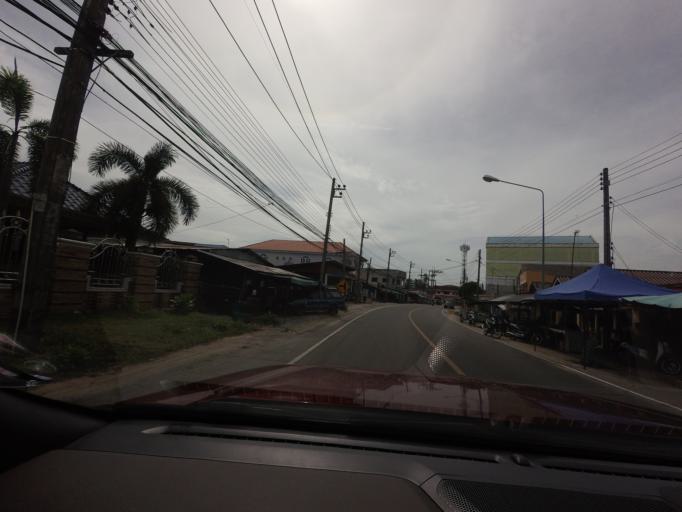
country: TH
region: Narathiwat
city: Tak Bai
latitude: 6.2382
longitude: 102.0856
